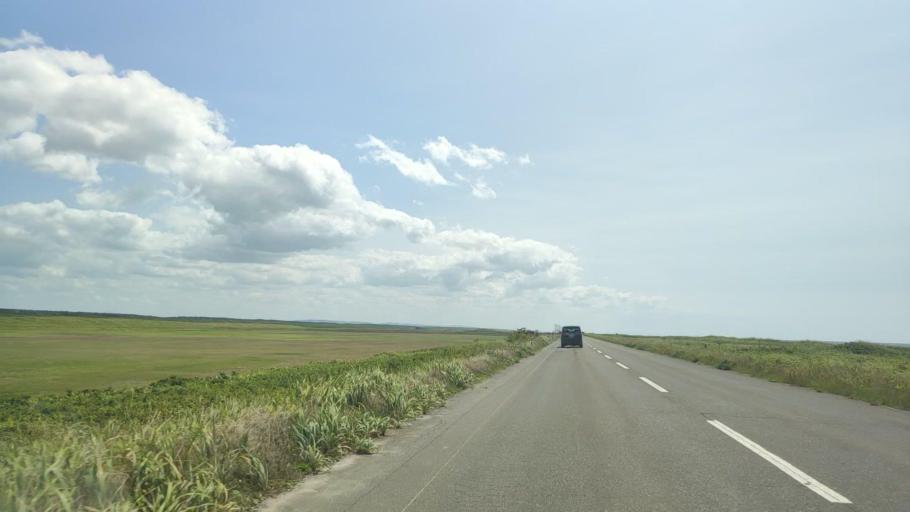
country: JP
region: Hokkaido
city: Makubetsu
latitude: 45.0379
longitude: 141.6606
